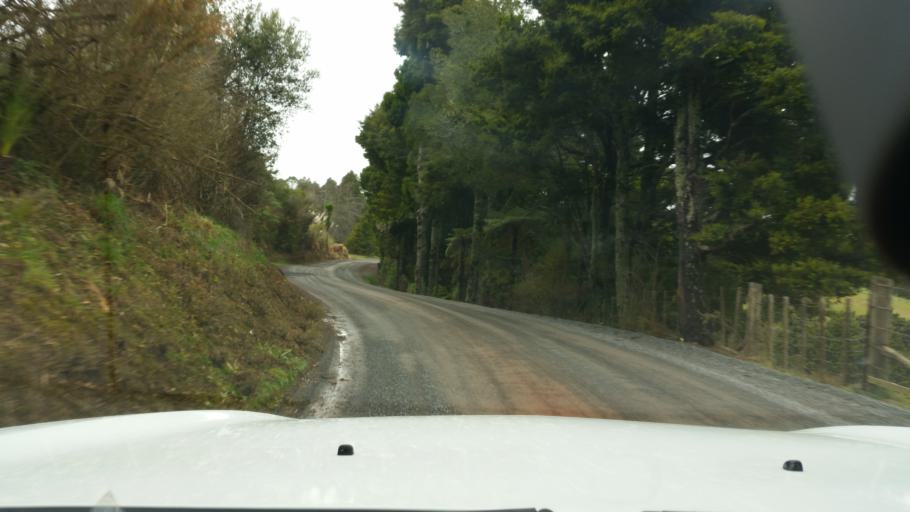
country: NZ
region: Northland
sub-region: Whangarei
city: Whangarei
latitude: -35.7318
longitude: 174.4247
